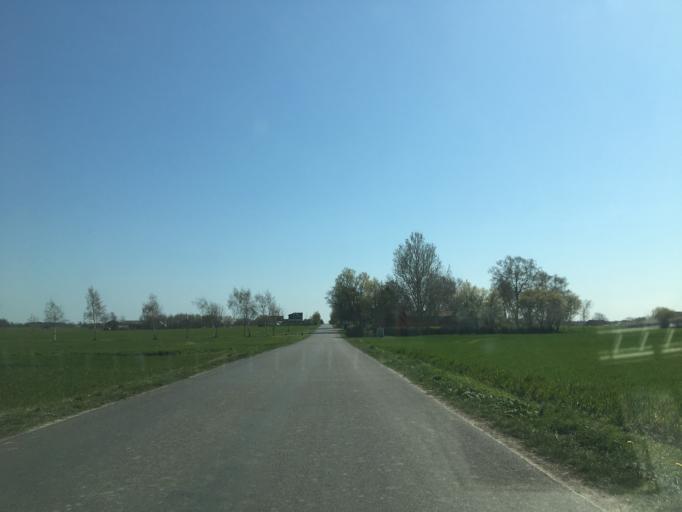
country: DK
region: Zealand
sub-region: Guldborgsund Kommune
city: Nykobing Falster
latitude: 54.7431
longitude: 11.7852
